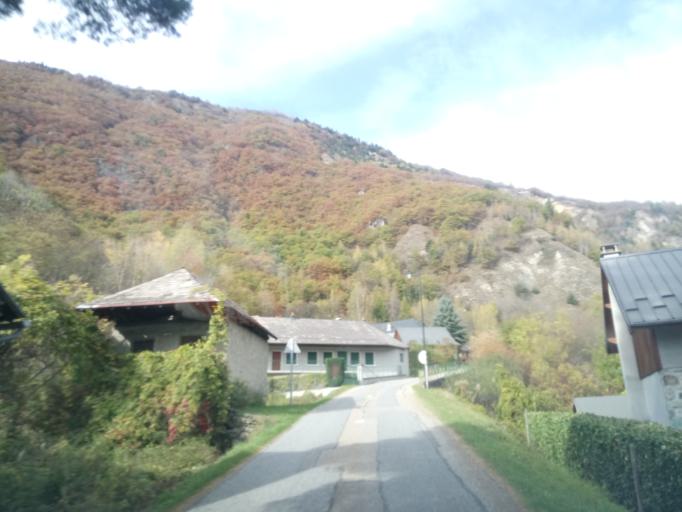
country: FR
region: Rhone-Alpes
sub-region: Departement de la Savoie
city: La Chambre
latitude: 45.3751
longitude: 6.3136
